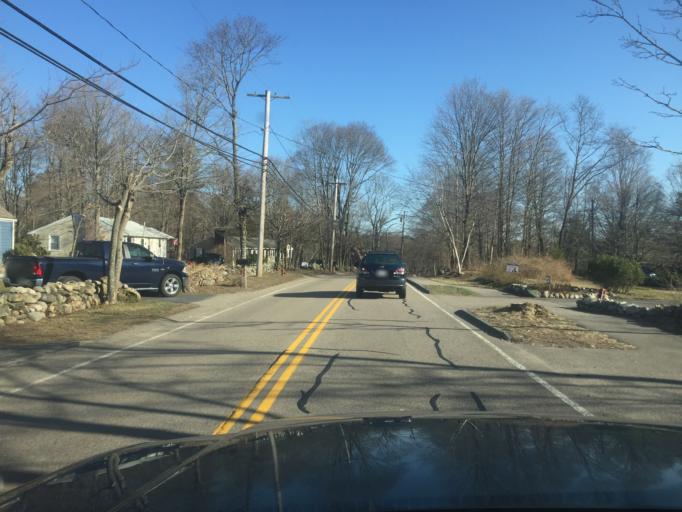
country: US
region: Massachusetts
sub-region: Norfolk County
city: Millis-Clicquot
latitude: 42.1443
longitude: -71.3568
